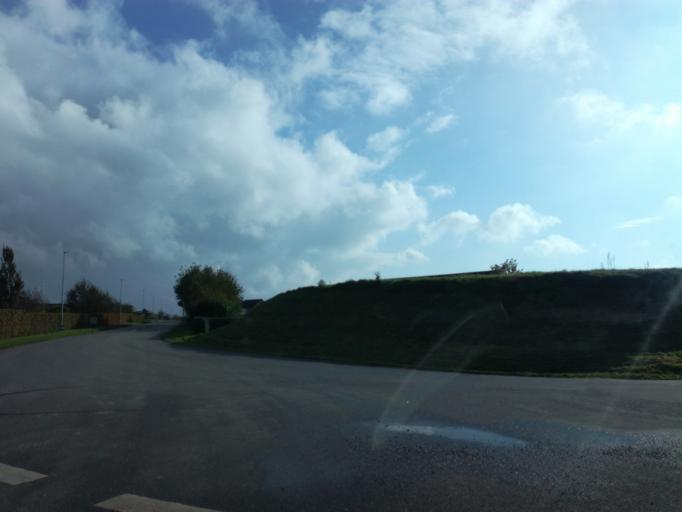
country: DK
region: South Denmark
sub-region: Vejle Kommune
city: Borkop
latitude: 55.6430
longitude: 9.6359
